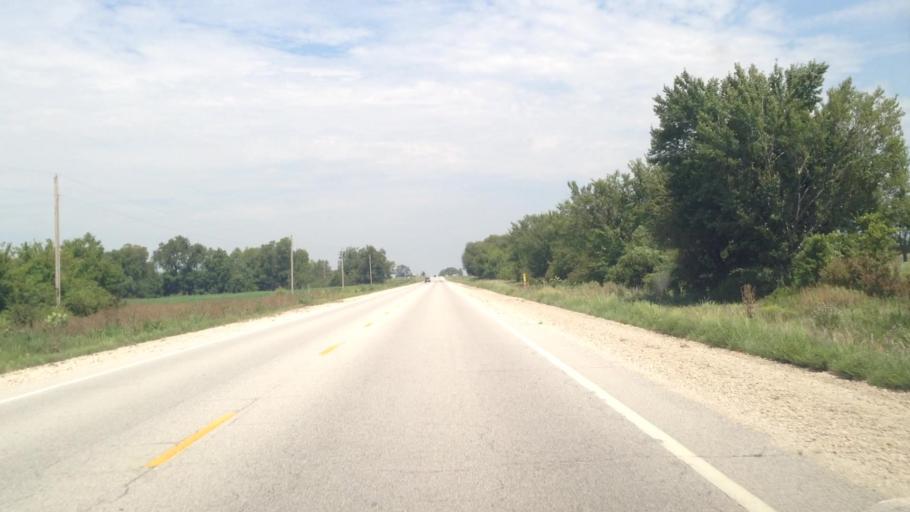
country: US
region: Kansas
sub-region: Neosho County
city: Erie
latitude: 37.4646
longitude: -95.2695
